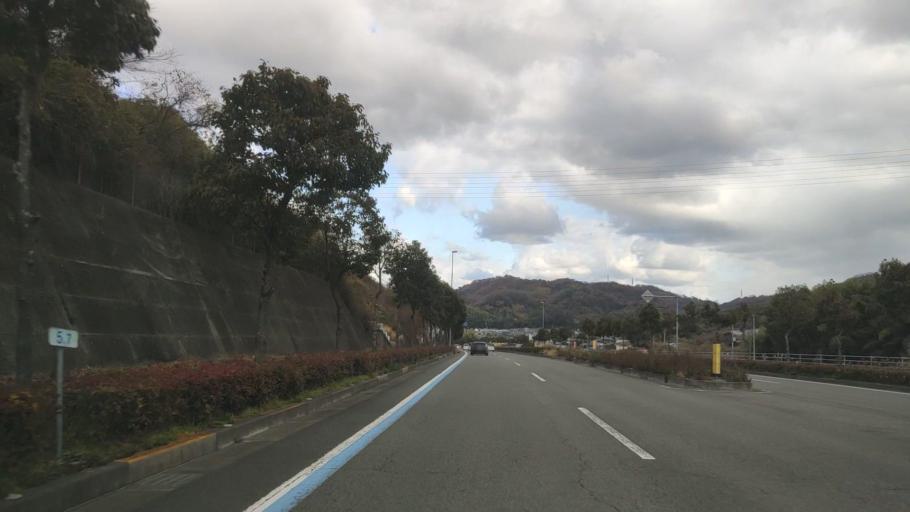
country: JP
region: Ehime
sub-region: Shikoku-chuo Shi
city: Matsuyama
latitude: 33.8918
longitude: 132.7574
